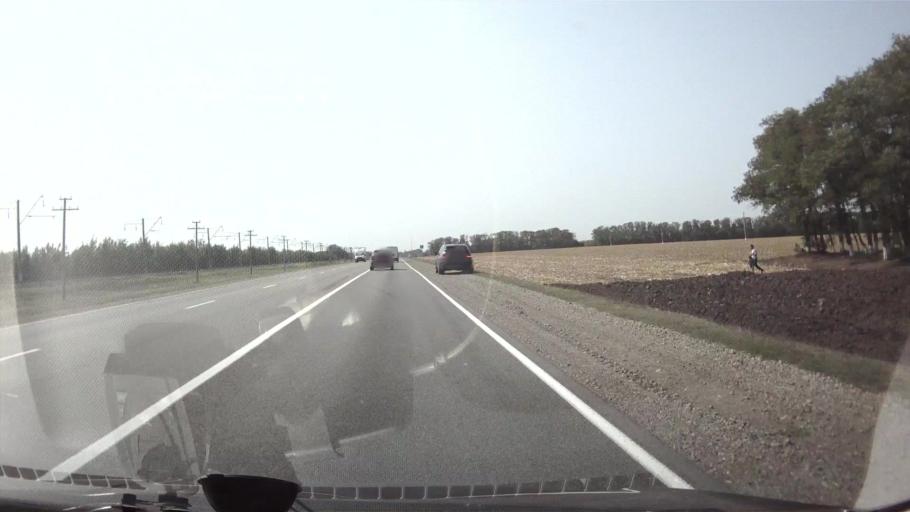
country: RU
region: Krasnodarskiy
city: Dvubratskiy
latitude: 45.2514
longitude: 39.7616
